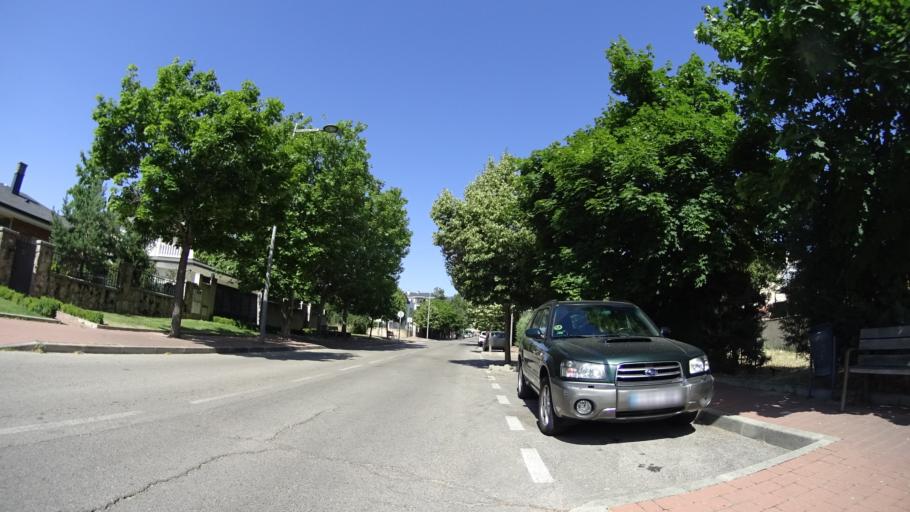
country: ES
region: Madrid
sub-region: Provincia de Madrid
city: Guadarrama
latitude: 40.6789
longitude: -4.0963
